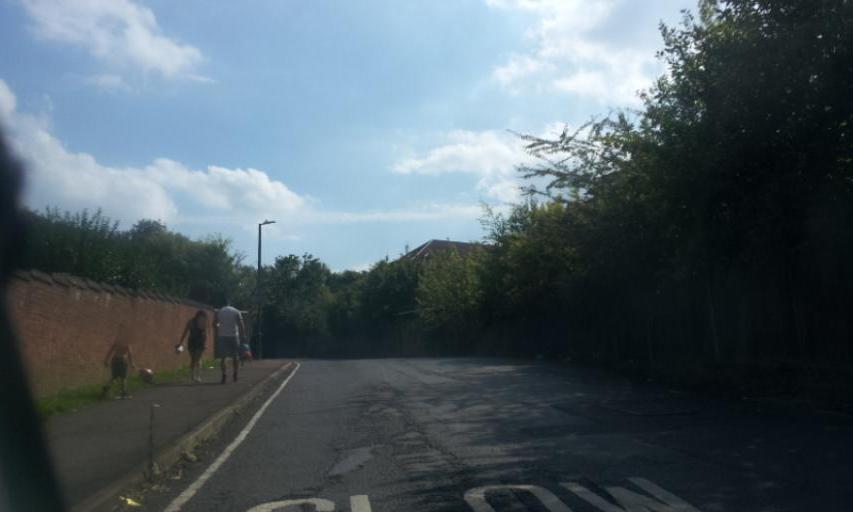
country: GB
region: England
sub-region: Kent
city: Maidstone
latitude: 51.2617
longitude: 0.5126
